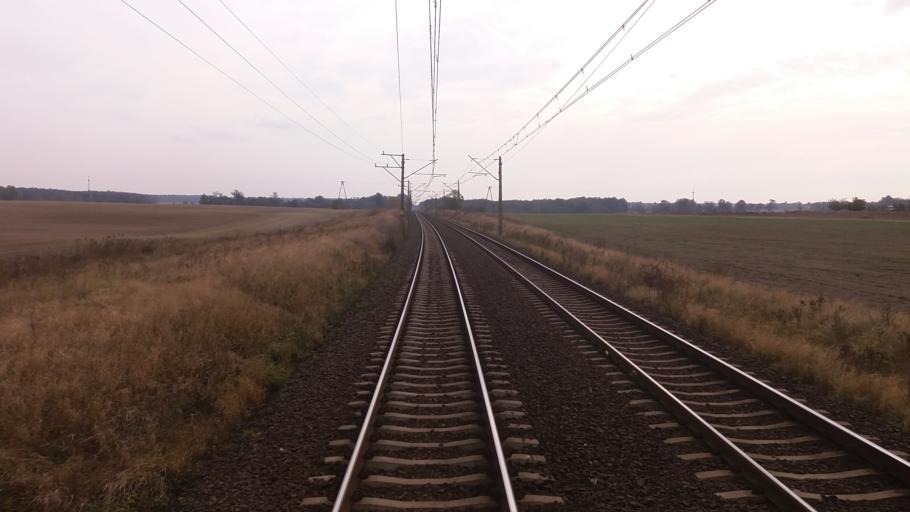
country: PL
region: West Pomeranian Voivodeship
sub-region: Powiat stargardzki
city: Dolice
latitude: 53.2303
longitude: 15.1380
